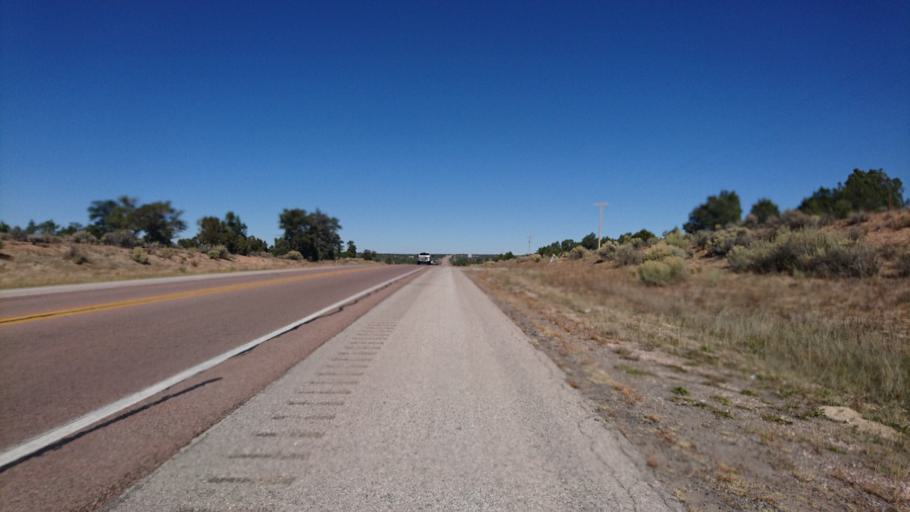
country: US
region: New Mexico
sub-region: McKinley County
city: Black Rock
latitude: 35.2758
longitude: -108.7549
